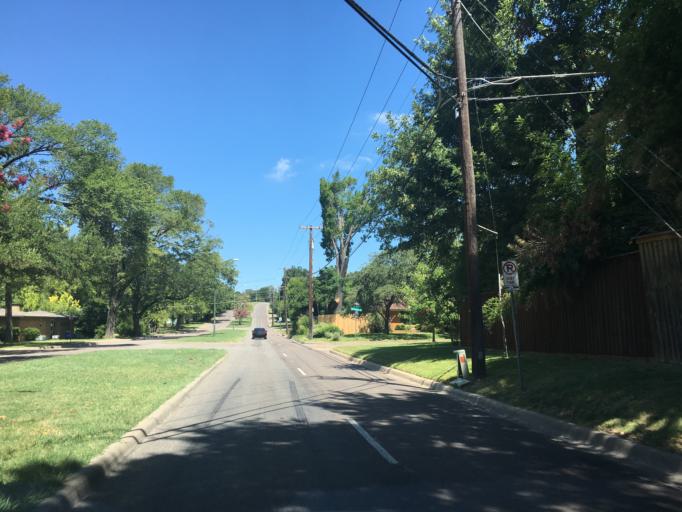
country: US
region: Texas
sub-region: Dallas County
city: Garland
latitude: 32.8455
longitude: -96.6938
